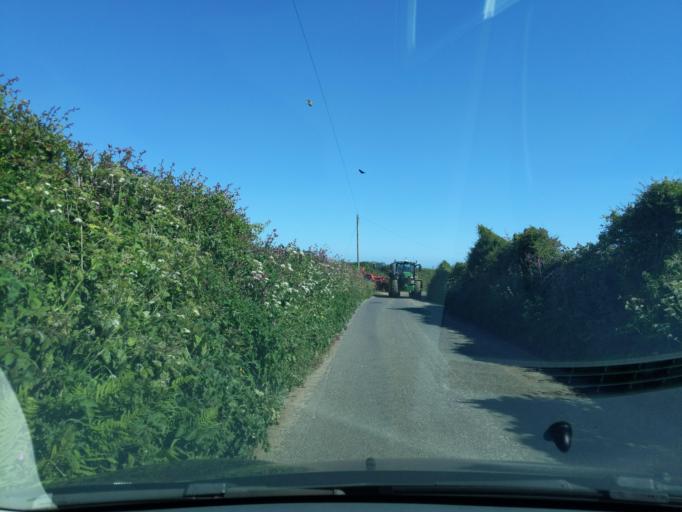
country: GB
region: England
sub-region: Cornwall
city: St. Buryan
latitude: 50.0725
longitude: -5.6138
